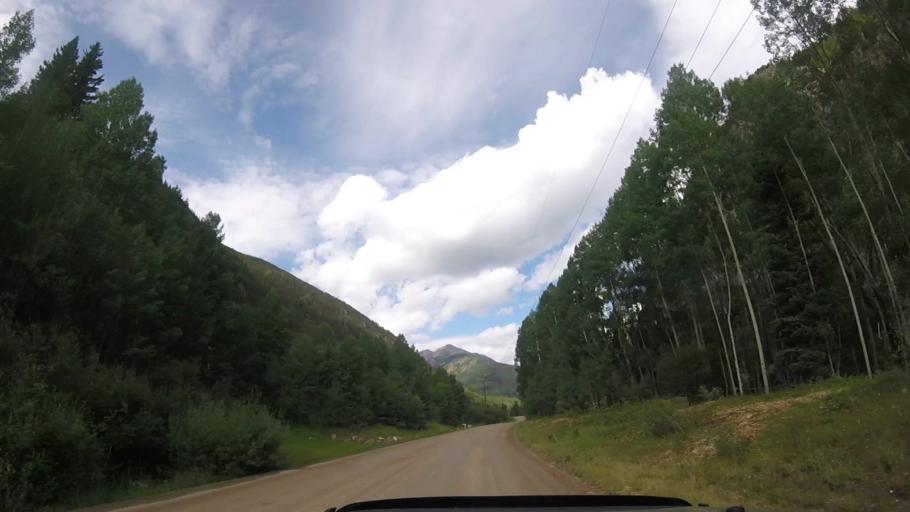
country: US
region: Colorado
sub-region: San Miguel County
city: Mountain Village
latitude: 37.8582
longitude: -107.8602
